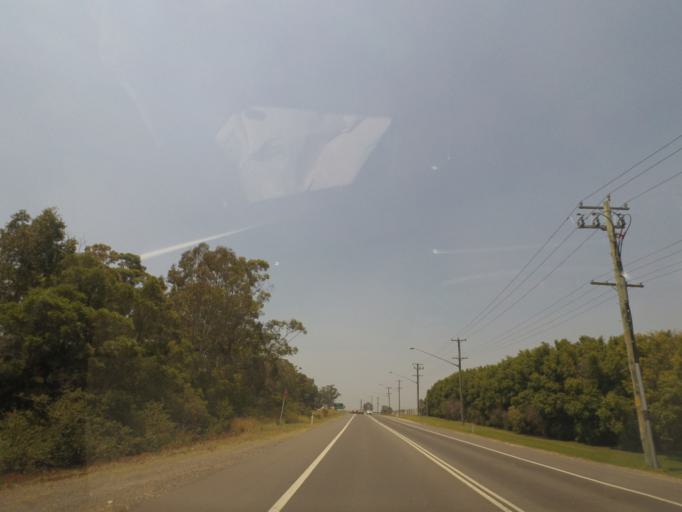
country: AU
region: New South Wales
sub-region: Newcastle
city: Beresfield
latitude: -32.8198
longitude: 151.6988
